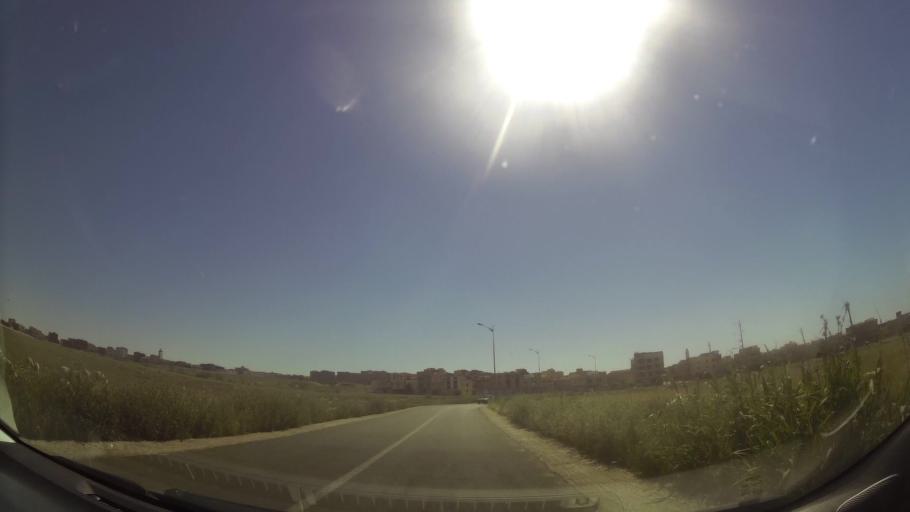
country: MA
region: Oriental
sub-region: Oujda-Angad
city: Oujda
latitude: 34.6922
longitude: -1.8665
